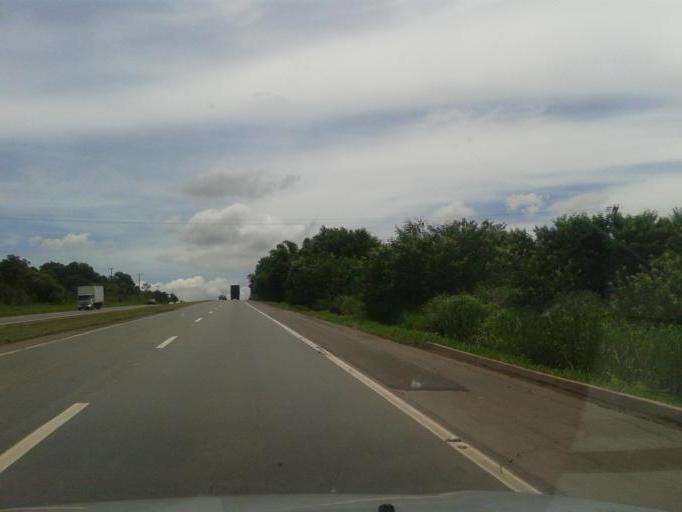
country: BR
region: Goias
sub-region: Aparecida De Goiania
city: Aparecida de Goiania
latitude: -16.8688
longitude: -49.2506
